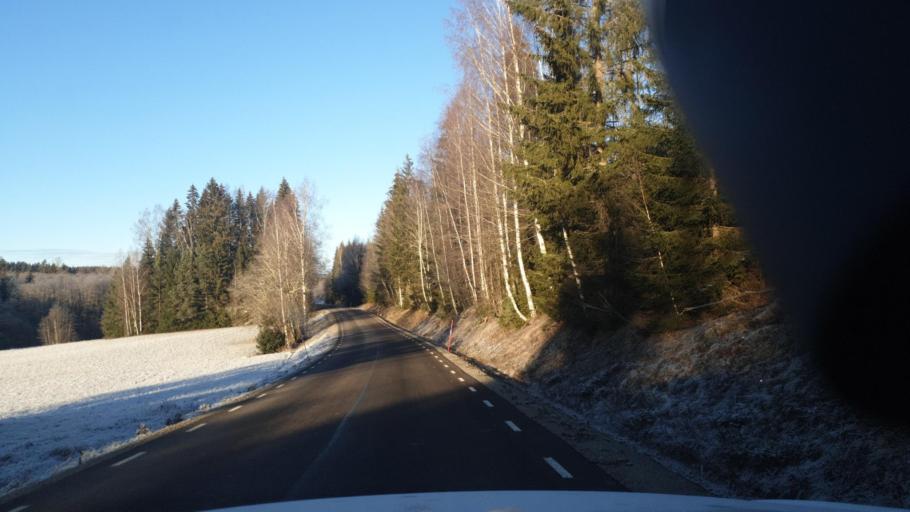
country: SE
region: Vaermland
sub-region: Sunne Kommun
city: Sunne
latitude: 59.6745
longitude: 12.9024
